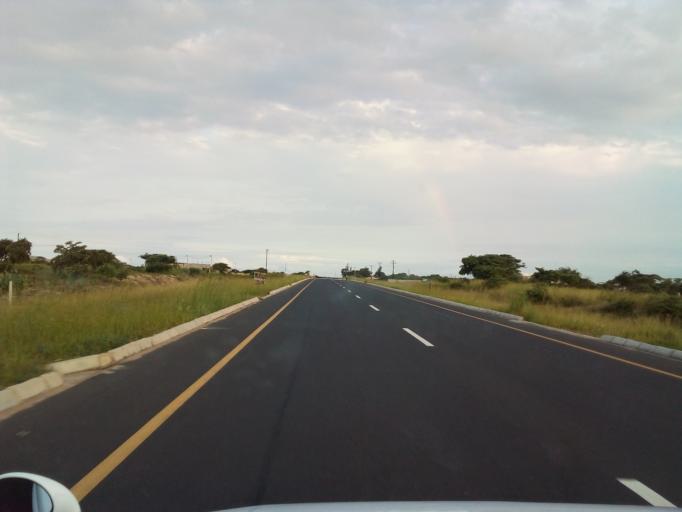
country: MZ
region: Maputo City
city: Maputo
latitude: -26.0475
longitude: 32.5739
